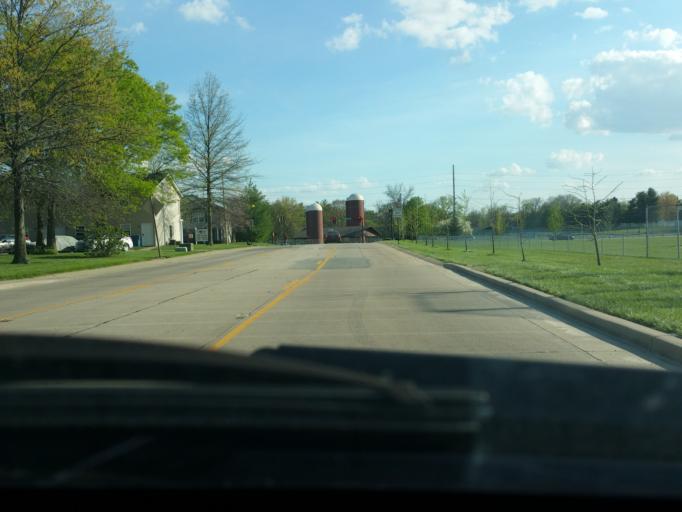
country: US
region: Illinois
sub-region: Madison County
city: Edwardsville
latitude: 38.7867
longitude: -89.9660
